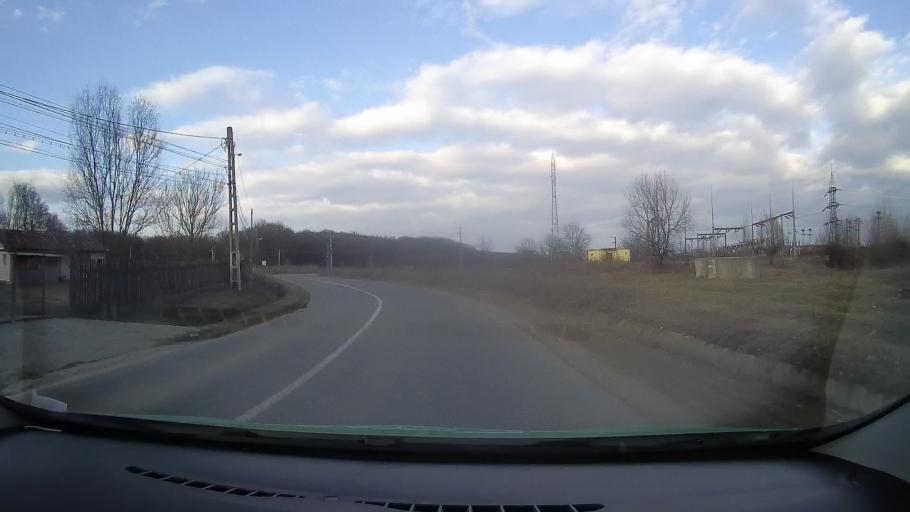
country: RO
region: Dambovita
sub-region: Comuna Gura Ocnitei
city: Gura Ocnitei
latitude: 44.9407
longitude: 25.5809
